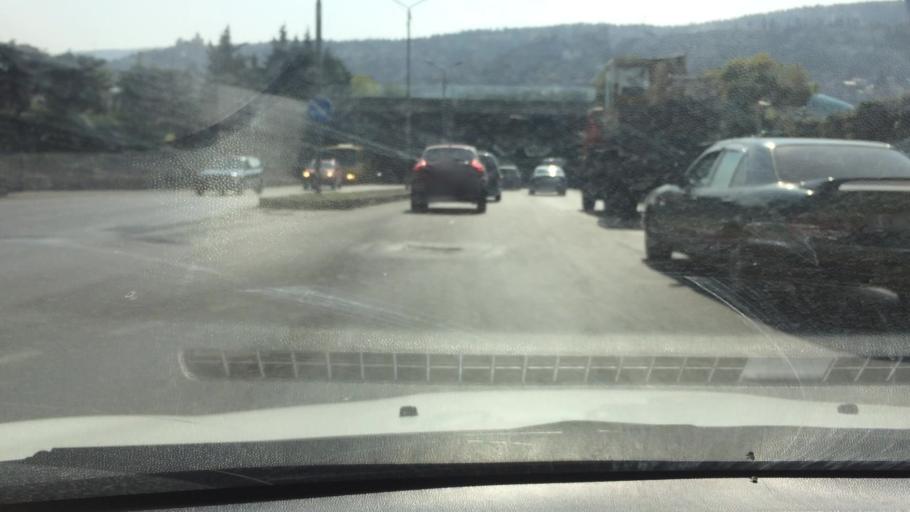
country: GE
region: T'bilisi
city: Tbilisi
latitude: 41.6955
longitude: 44.8090
